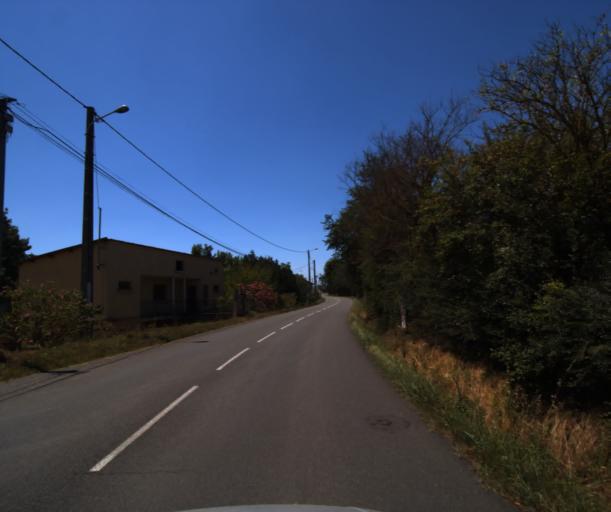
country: FR
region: Midi-Pyrenees
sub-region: Departement de la Haute-Garonne
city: Muret
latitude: 43.4599
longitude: 1.3143
